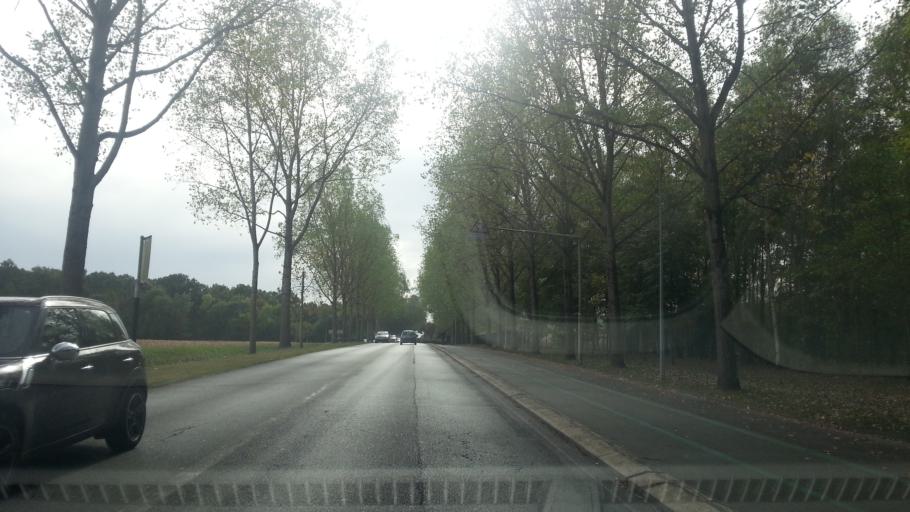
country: FR
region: Picardie
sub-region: Departement de l'Oise
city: Senlis
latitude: 49.1935
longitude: 2.5756
